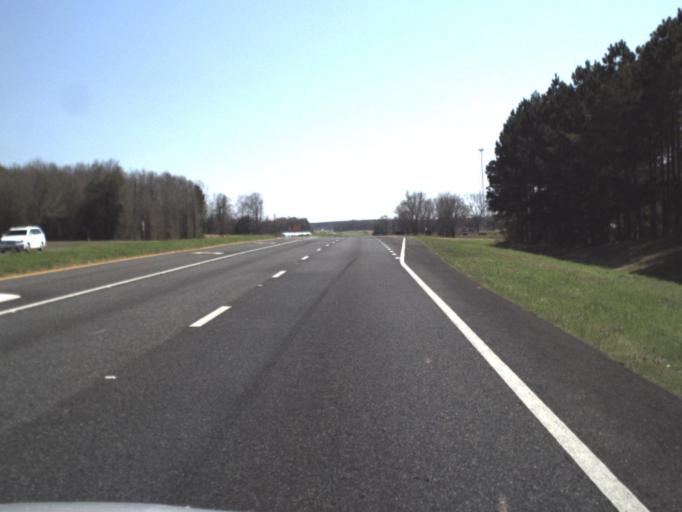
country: US
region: Florida
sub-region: Jackson County
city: Marianna
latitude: 30.8739
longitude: -85.3616
